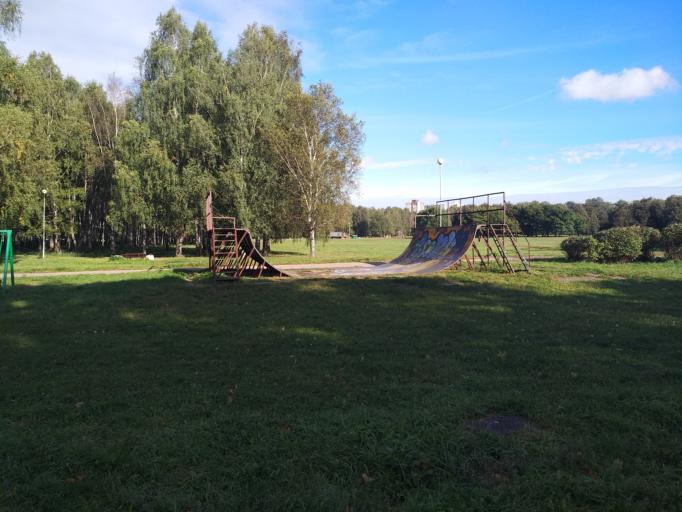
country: BY
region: Minsk
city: Minsk
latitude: 53.9303
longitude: 27.5669
